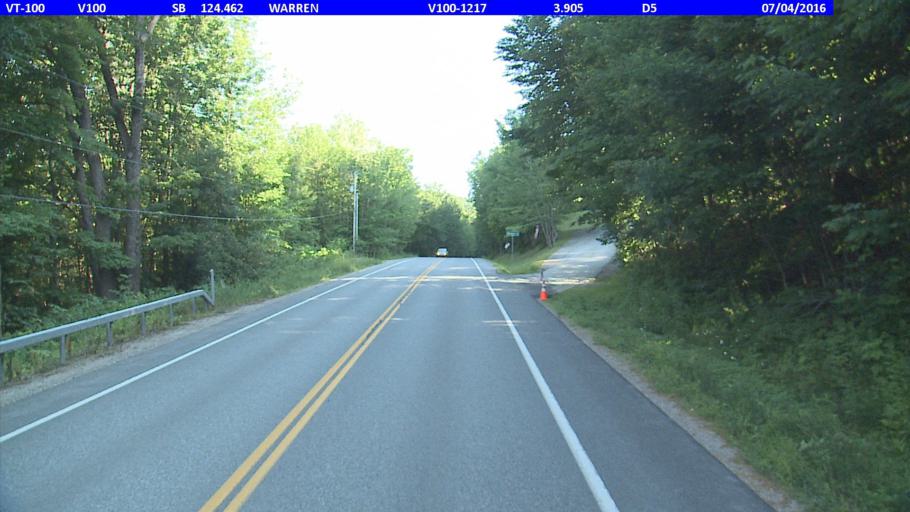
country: US
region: Vermont
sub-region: Washington County
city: Northfield
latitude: 44.1145
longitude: -72.8579
